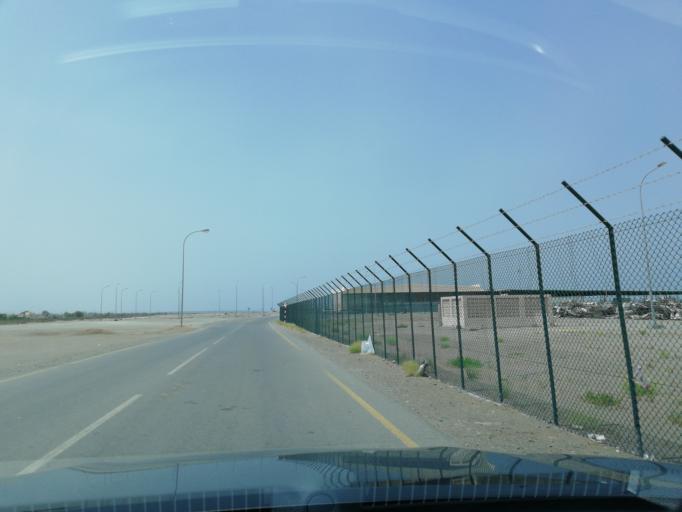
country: OM
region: Al Batinah
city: Shinas
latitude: 24.7463
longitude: 56.4698
